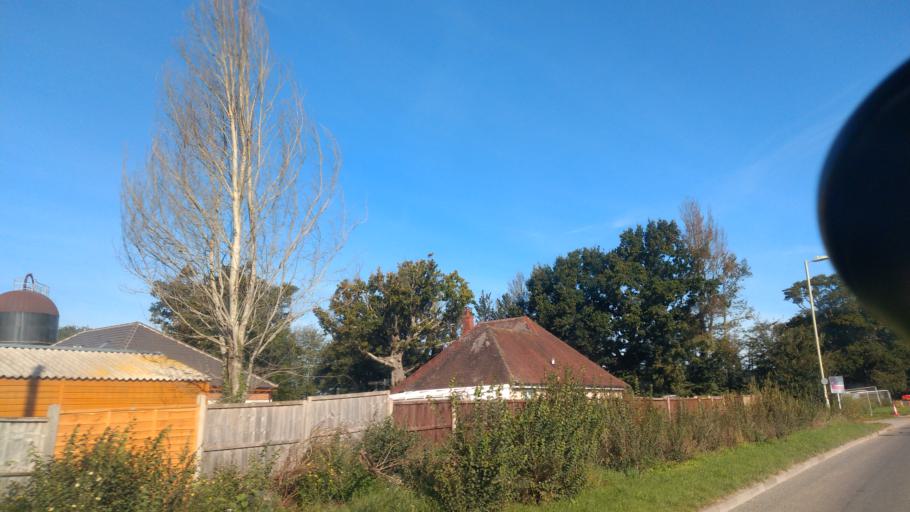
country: GB
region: England
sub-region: Hampshire
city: Lee-on-the-Solent
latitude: 50.8407
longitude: -1.2265
